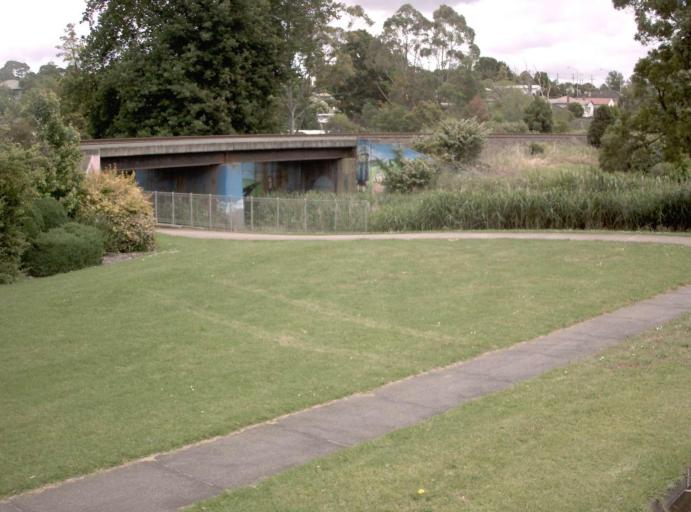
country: AU
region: Victoria
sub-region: Baw Baw
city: Warragul
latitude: -38.1603
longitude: 145.9234
